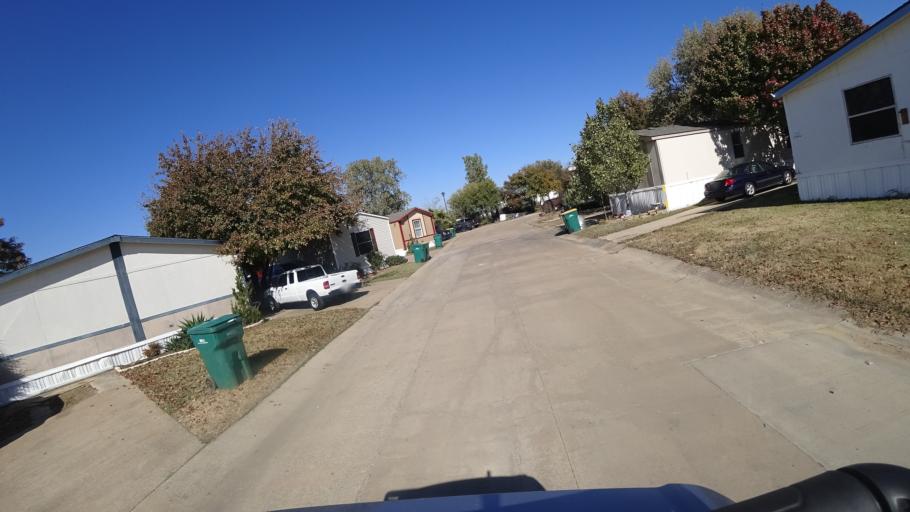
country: US
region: Texas
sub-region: Denton County
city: Lewisville
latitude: 33.0407
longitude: -96.9342
